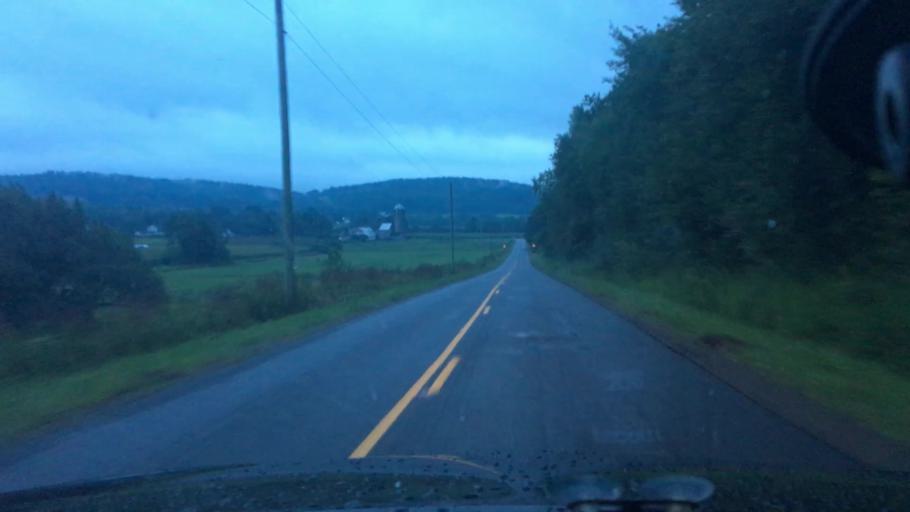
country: US
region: New York
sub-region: Cattaraugus County
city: Little Valley
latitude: 42.2396
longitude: -78.8889
